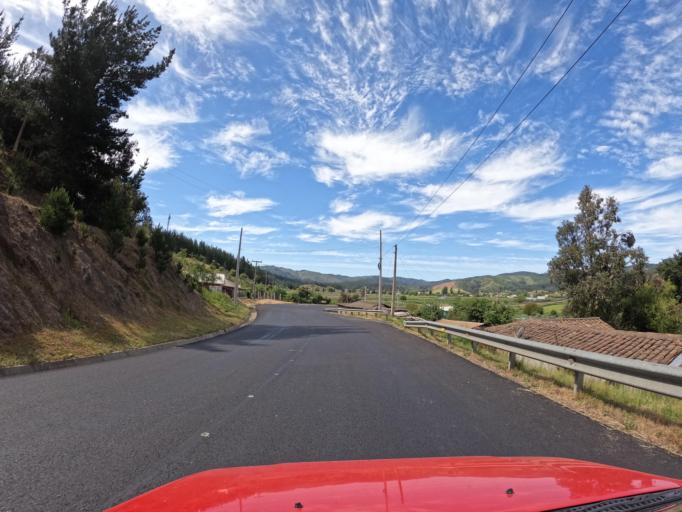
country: CL
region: Maule
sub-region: Provincia de Talca
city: Constitucion
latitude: -35.0737
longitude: -72.0327
